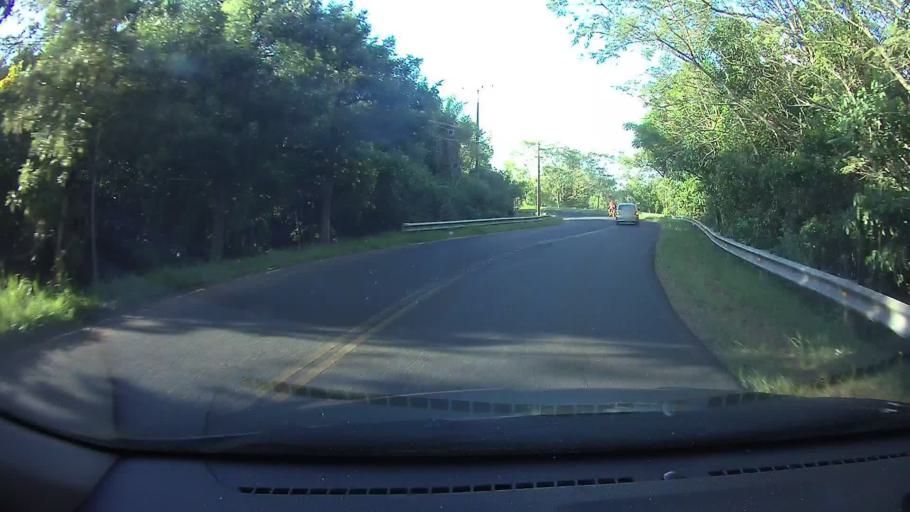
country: PY
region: Cordillera
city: Altos
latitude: -25.1659
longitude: -57.2339
